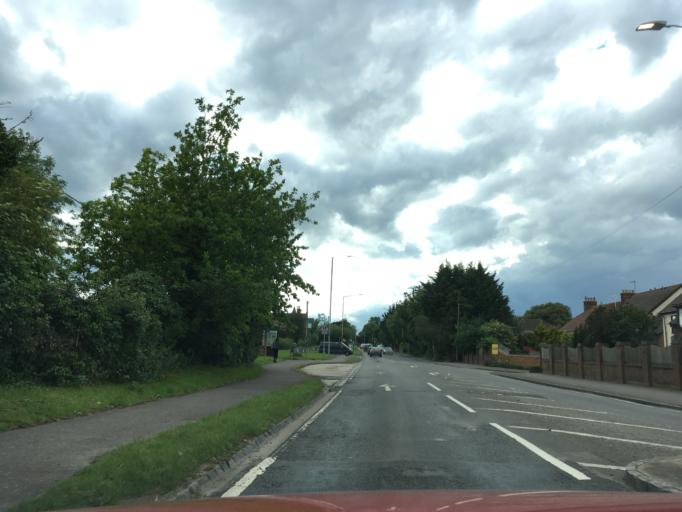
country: GB
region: England
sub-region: Buckinghamshire
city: Stone
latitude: 51.8038
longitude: -0.8547
